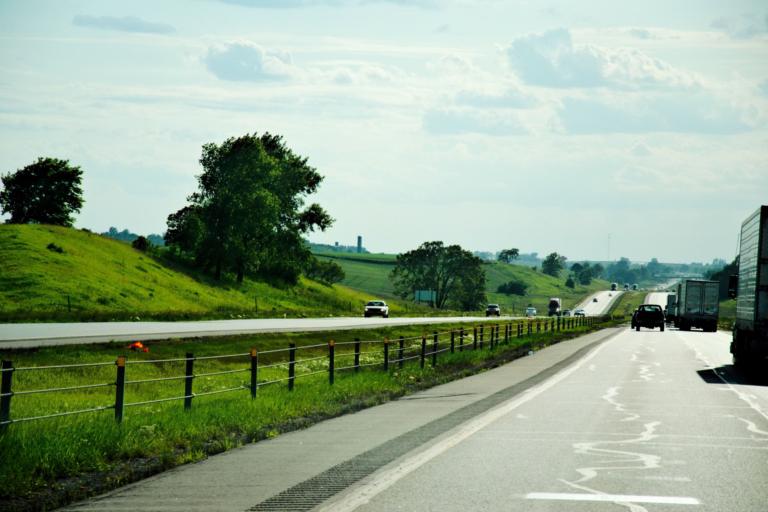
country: US
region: Iowa
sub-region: Jasper County
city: Newton
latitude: 41.6821
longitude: -93.0883
